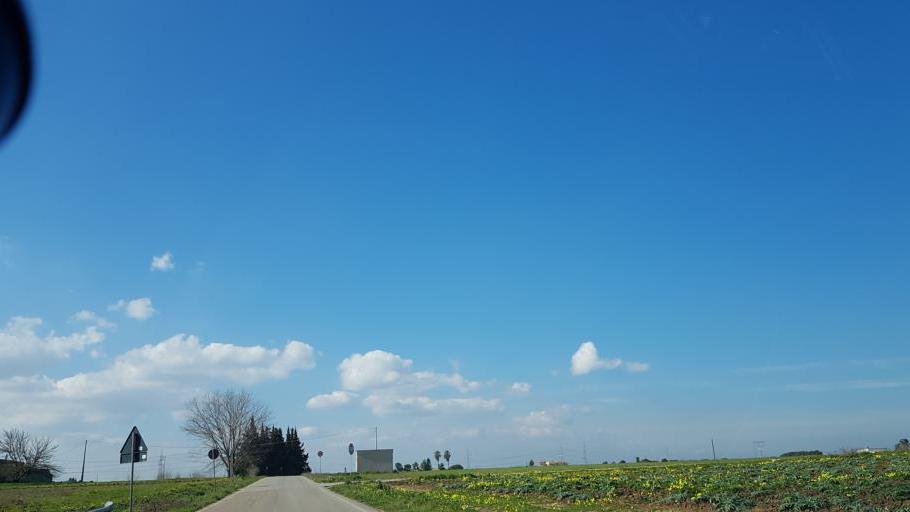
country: IT
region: Apulia
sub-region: Provincia di Brindisi
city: La Rosa
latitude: 40.5920
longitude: 17.9178
